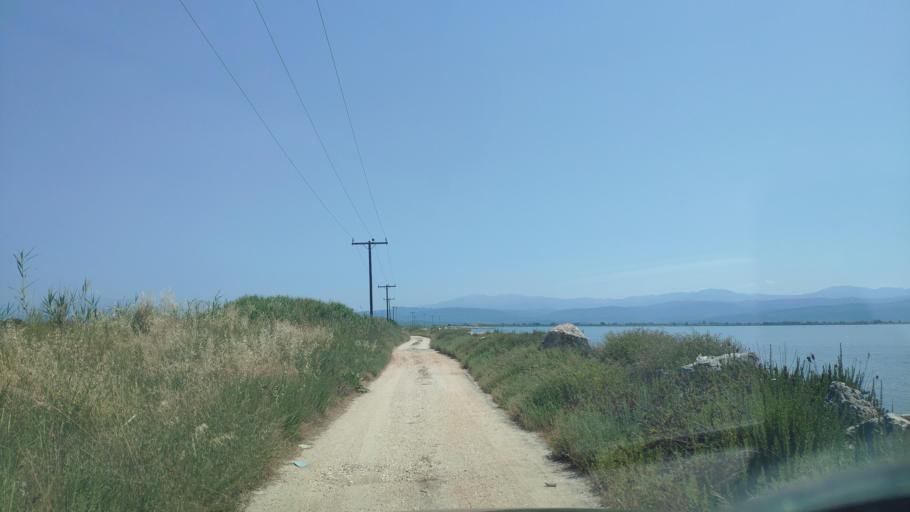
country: GR
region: Epirus
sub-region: Nomos Artas
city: Aneza
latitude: 39.0229
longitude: 20.9362
